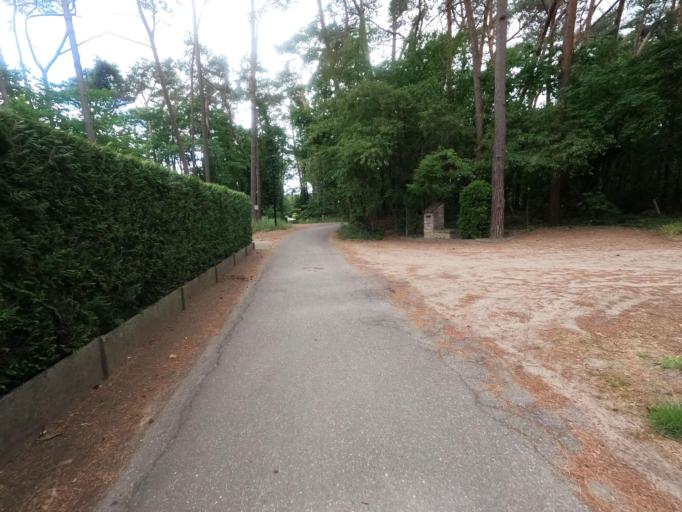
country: BE
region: Flanders
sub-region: Provincie Vlaams-Brabant
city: Tremelo
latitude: 50.9960
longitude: 4.7165
